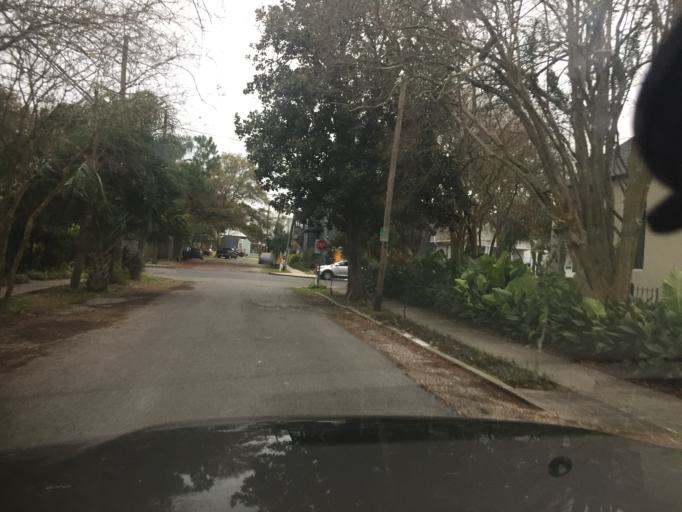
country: US
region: Louisiana
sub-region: Orleans Parish
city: New Orleans
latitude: 29.9801
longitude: -90.0797
